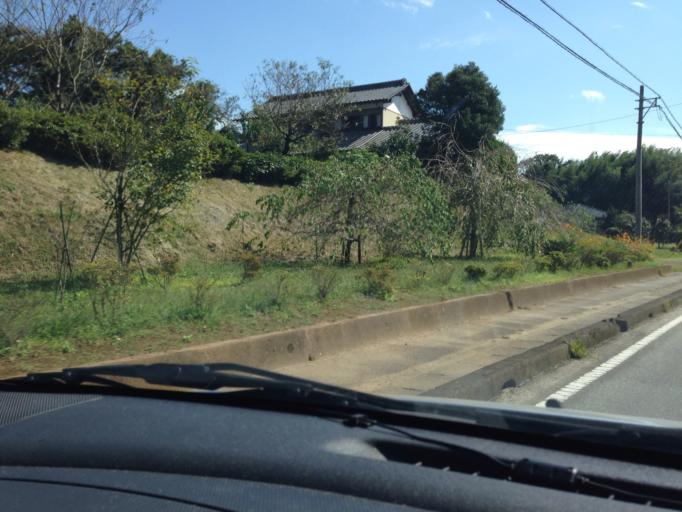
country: JP
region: Ibaraki
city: Inashiki
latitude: 36.0179
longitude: 140.2966
